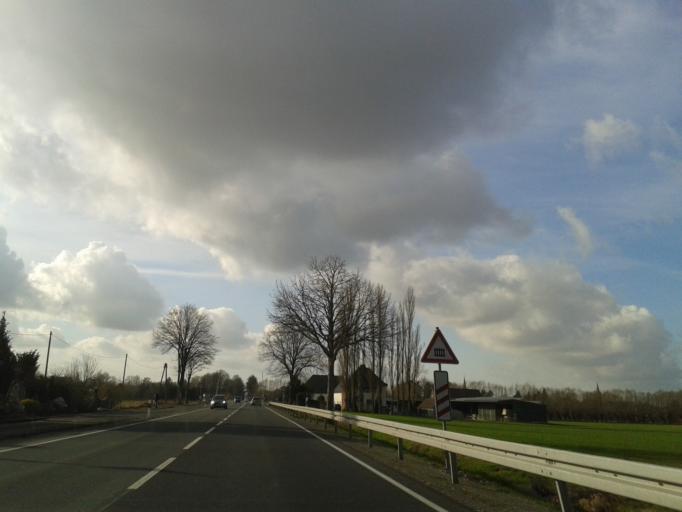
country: DE
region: North Rhine-Westphalia
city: Geseke
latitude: 51.6420
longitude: 8.5289
